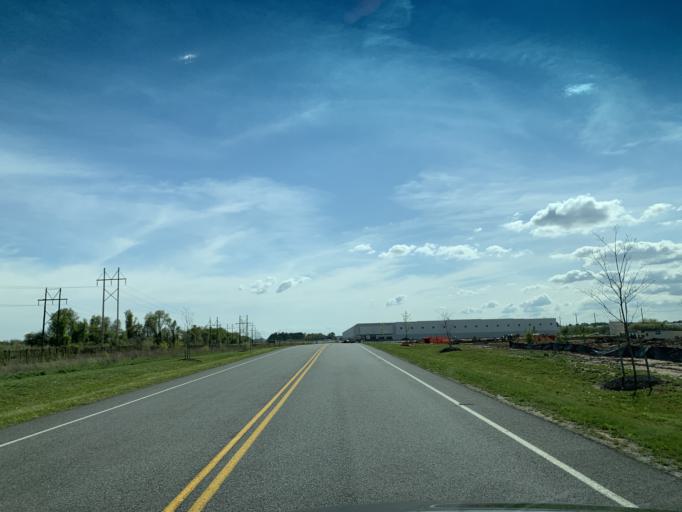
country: US
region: Maryland
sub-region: Harford County
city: Perryman
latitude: 39.4748
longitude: -76.1876
